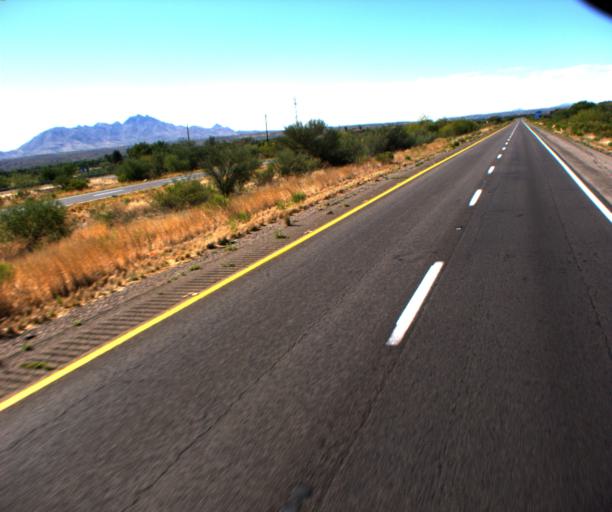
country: US
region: Arizona
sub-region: Santa Cruz County
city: Tubac
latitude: 31.6185
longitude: -111.0537
